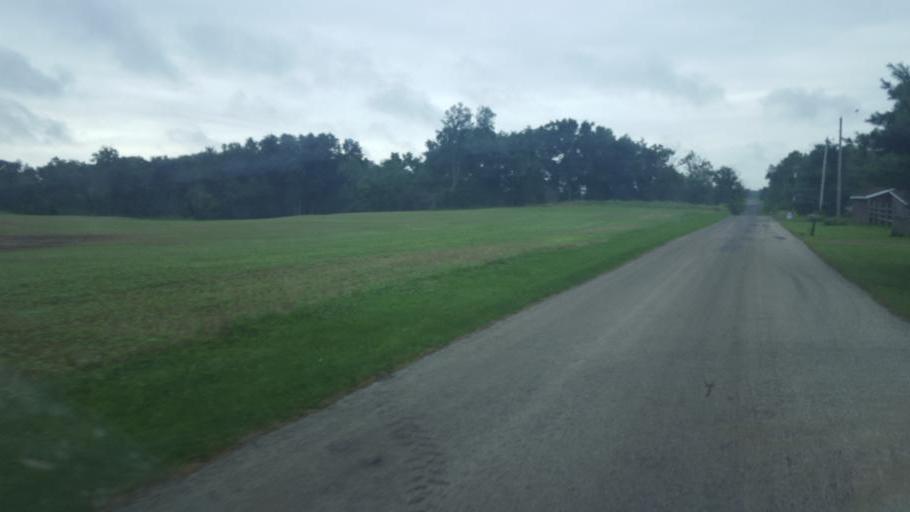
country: US
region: Ohio
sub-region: Knox County
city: Centerburg
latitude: 40.3938
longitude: -82.7412
